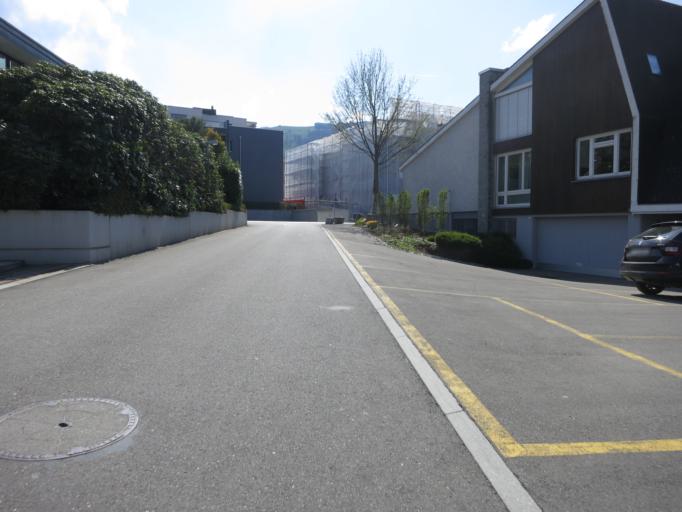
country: CH
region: Schwyz
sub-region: Bezirk March
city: Lachen
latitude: 47.1879
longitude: 8.8528
